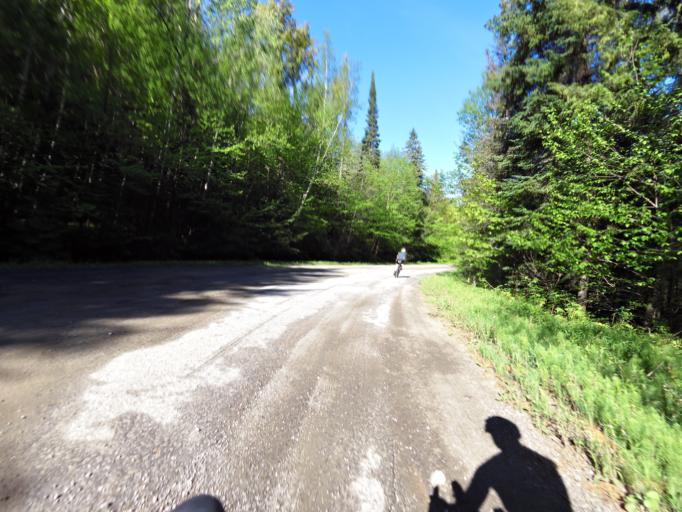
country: CA
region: Quebec
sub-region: Outaouais
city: Wakefield
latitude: 45.6109
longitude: -75.8654
